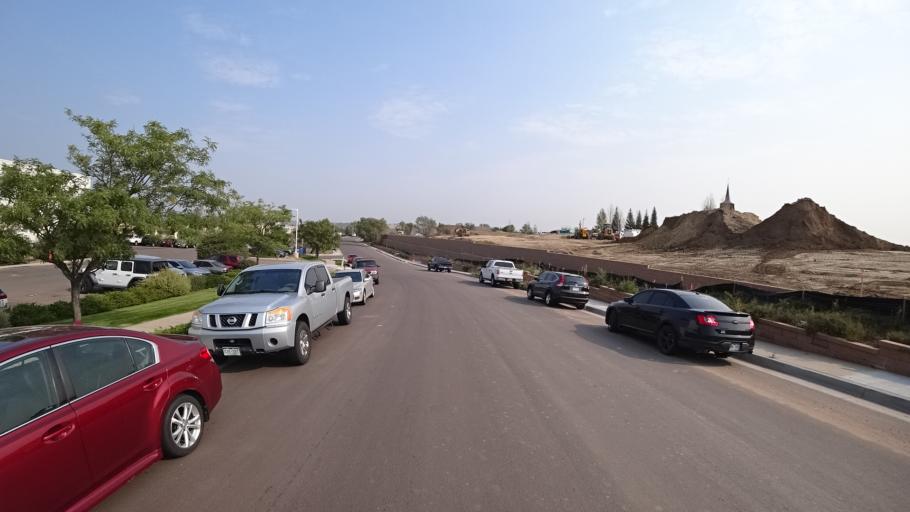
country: US
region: Colorado
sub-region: El Paso County
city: Stratmoor
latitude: 38.8172
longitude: -104.7536
